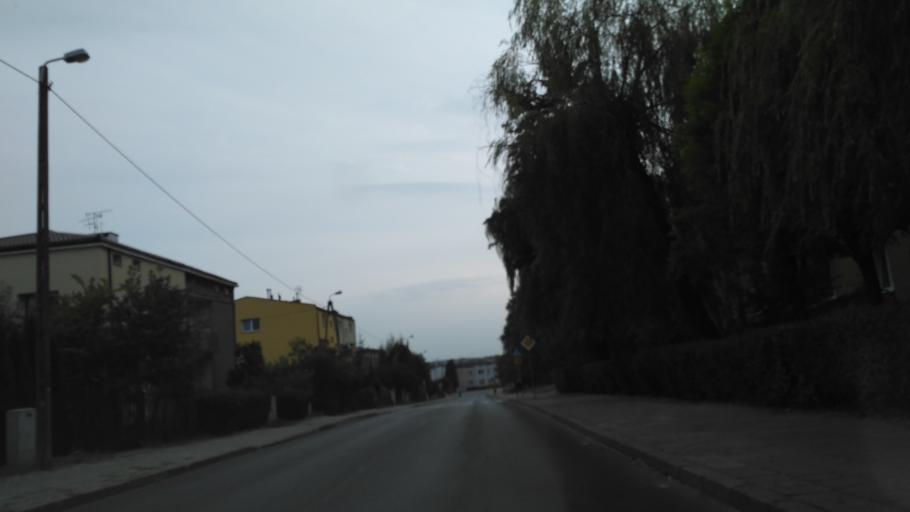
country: PL
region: Lublin Voivodeship
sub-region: Powiat lubelski
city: Lublin
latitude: 51.2287
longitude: 22.5952
